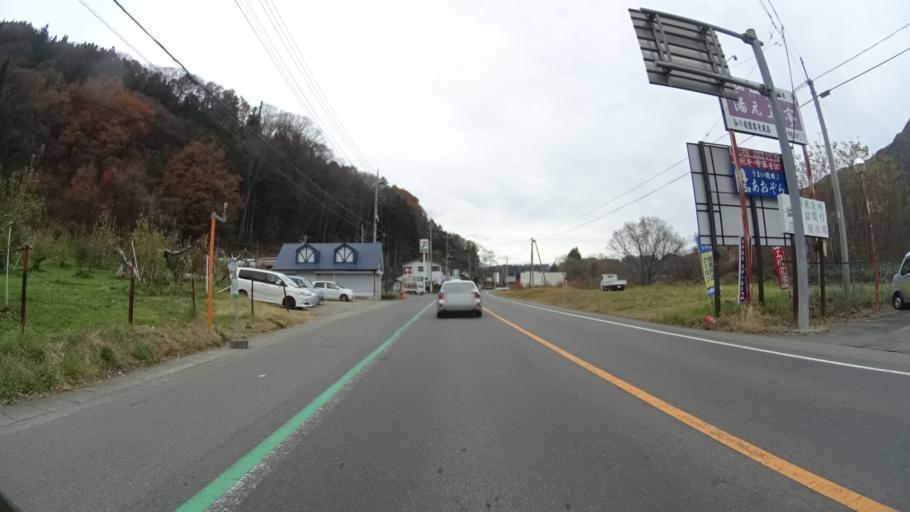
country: JP
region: Gunma
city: Numata
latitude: 36.6887
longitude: 139.2075
